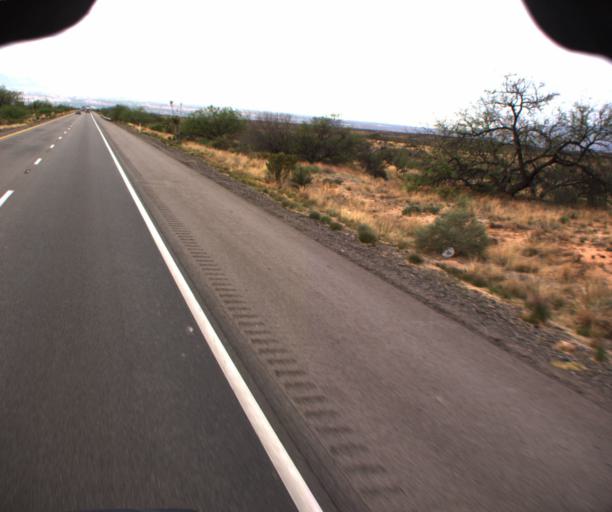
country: US
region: Arizona
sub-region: Cochise County
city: Saint David
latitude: 31.9902
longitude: -110.1833
